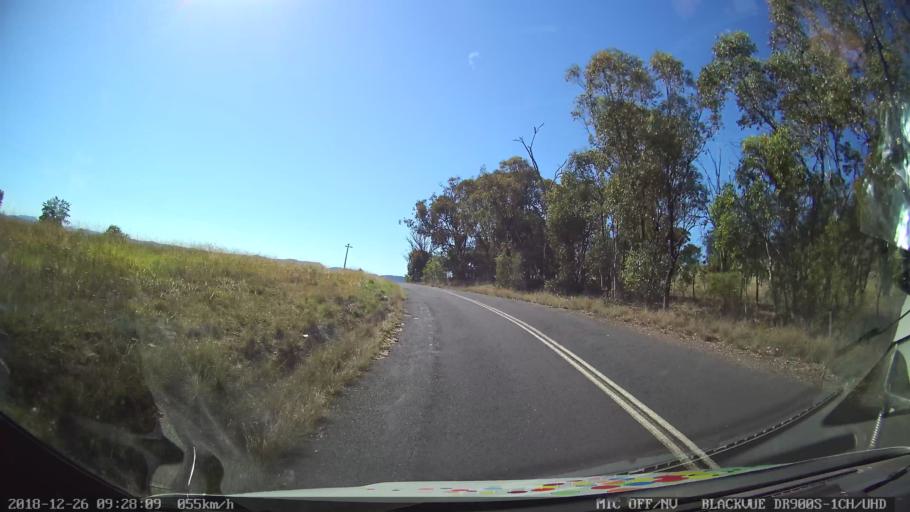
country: AU
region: New South Wales
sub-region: Mid-Western Regional
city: Kandos
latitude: -32.8425
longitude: 150.0204
